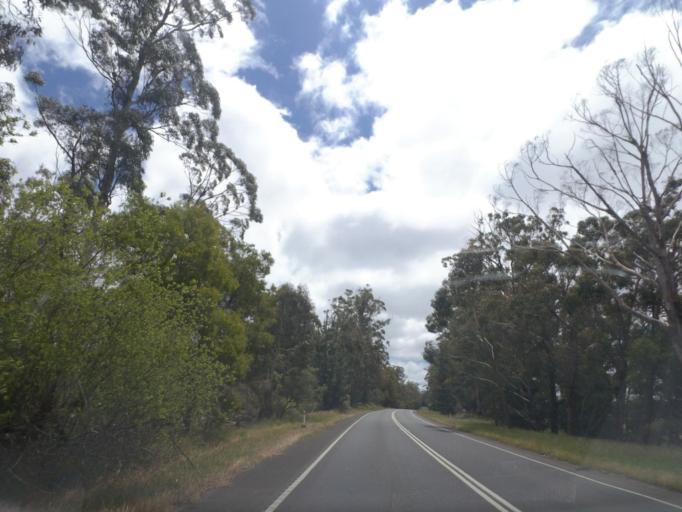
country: AU
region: Victoria
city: Brown Hill
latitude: -37.4909
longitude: 144.1542
